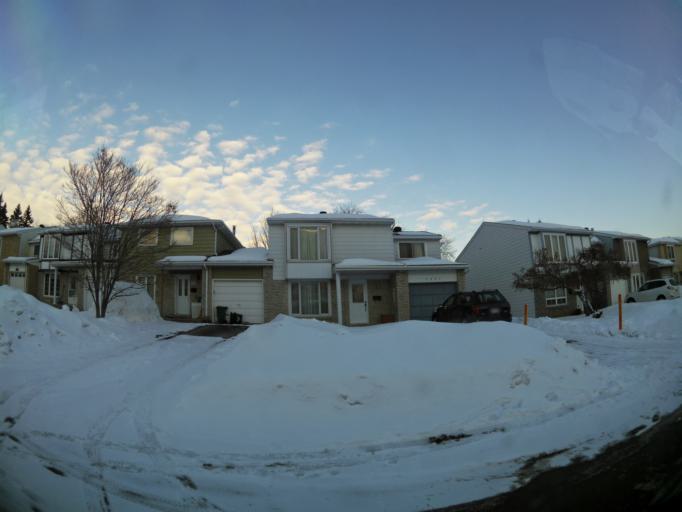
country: CA
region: Ontario
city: Ottawa
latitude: 45.4351
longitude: -75.5526
